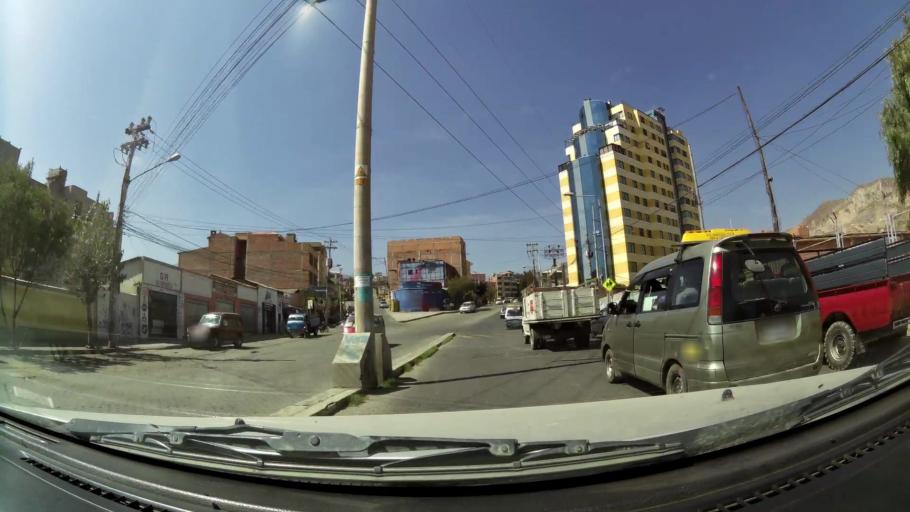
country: BO
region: La Paz
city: La Paz
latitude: -16.5407
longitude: -68.0638
